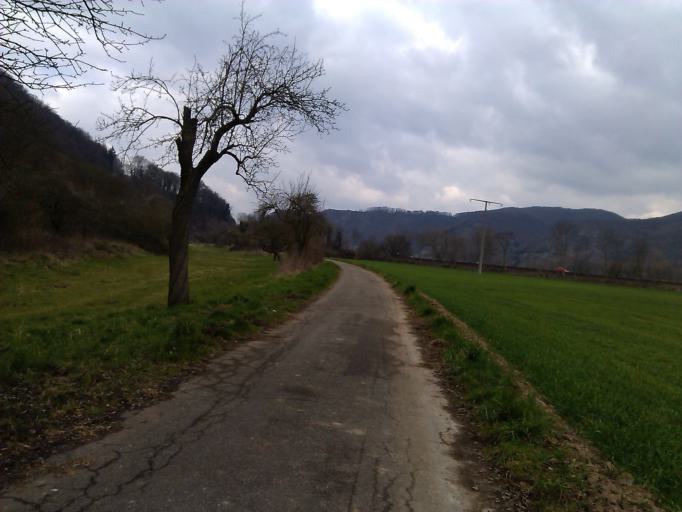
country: DE
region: Rheinland-Pfalz
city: Hammerstein
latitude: 50.4655
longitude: 7.3486
